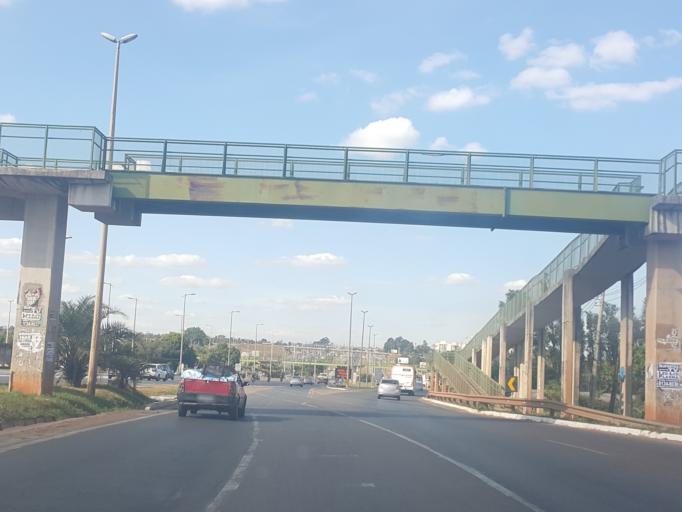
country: BR
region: Federal District
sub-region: Brasilia
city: Brasilia
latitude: -15.8167
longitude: -48.0097
